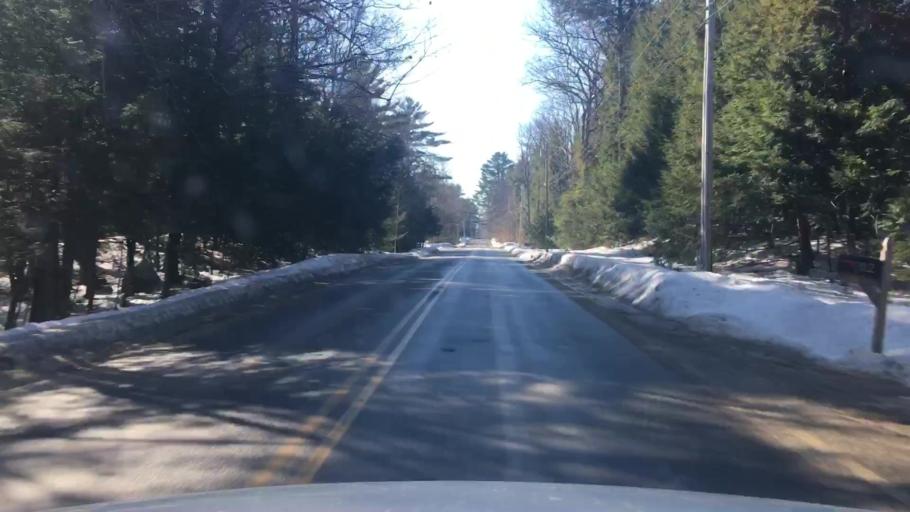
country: US
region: Maine
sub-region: Cumberland County
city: North Windham
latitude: 43.8450
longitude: -70.3567
